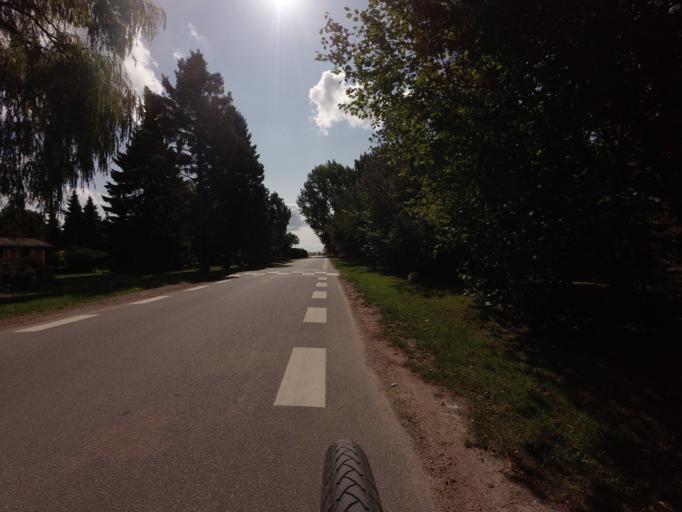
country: DK
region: Zealand
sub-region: Vordingborg Kommune
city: Stege
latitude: 54.9660
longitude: 12.3891
